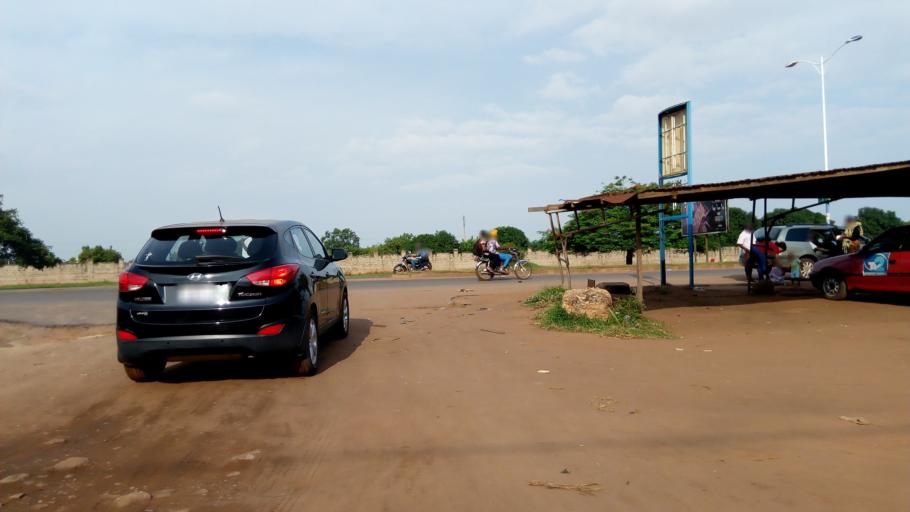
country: TG
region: Maritime
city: Lome
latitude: 6.2145
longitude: 1.2084
